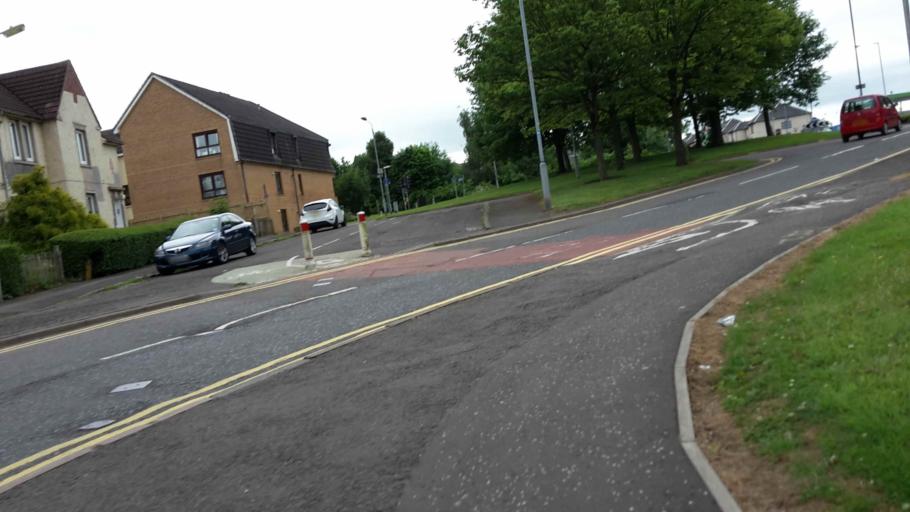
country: GB
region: Scotland
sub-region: South Lanarkshire
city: High Blantyre
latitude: 55.7930
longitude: -4.0854
